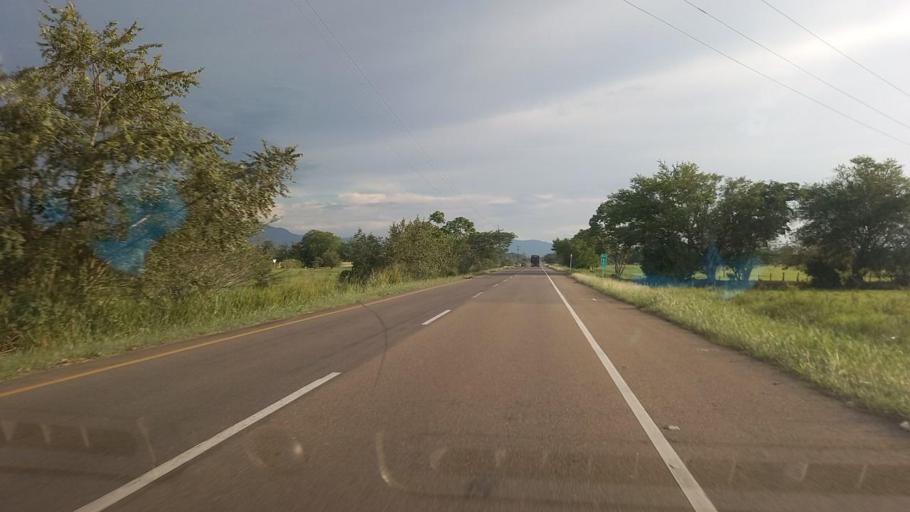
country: CO
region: Cundinamarca
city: Puerto Salgar
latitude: 5.5946
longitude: -74.6226
